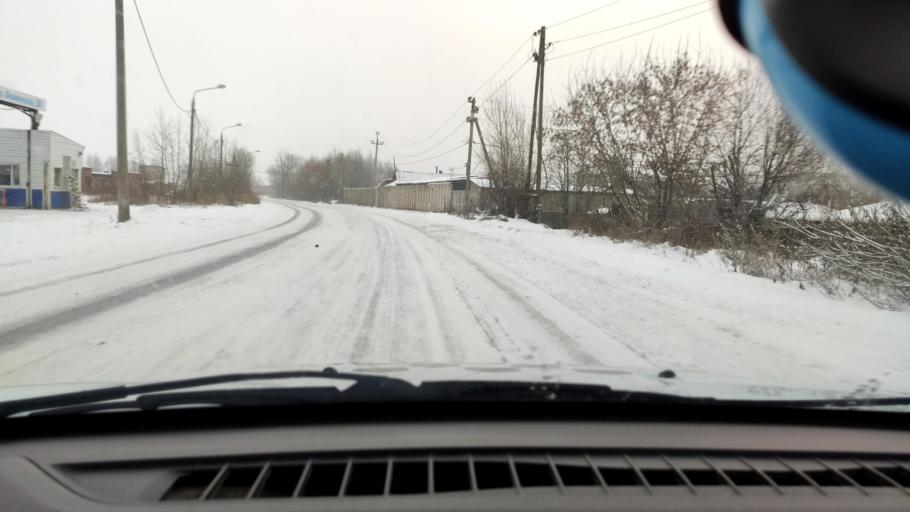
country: RU
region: Perm
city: Kondratovo
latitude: 58.0077
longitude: 56.1061
